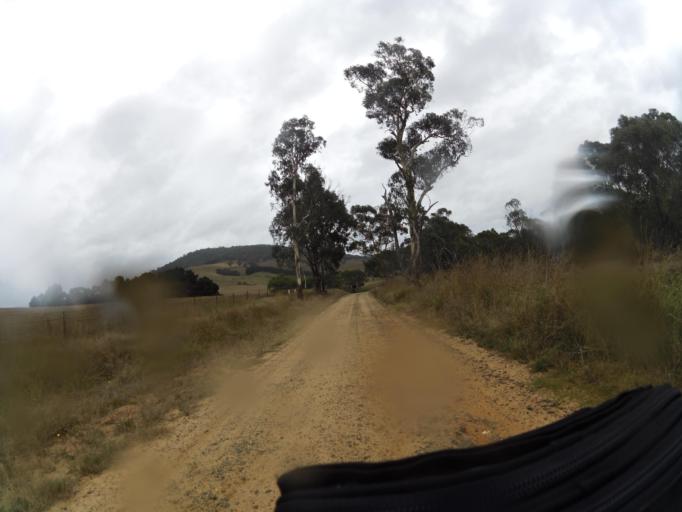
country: AU
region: New South Wales
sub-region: Greater Hume Shire
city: Holbrook
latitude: -36.2395
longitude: 147.6393
